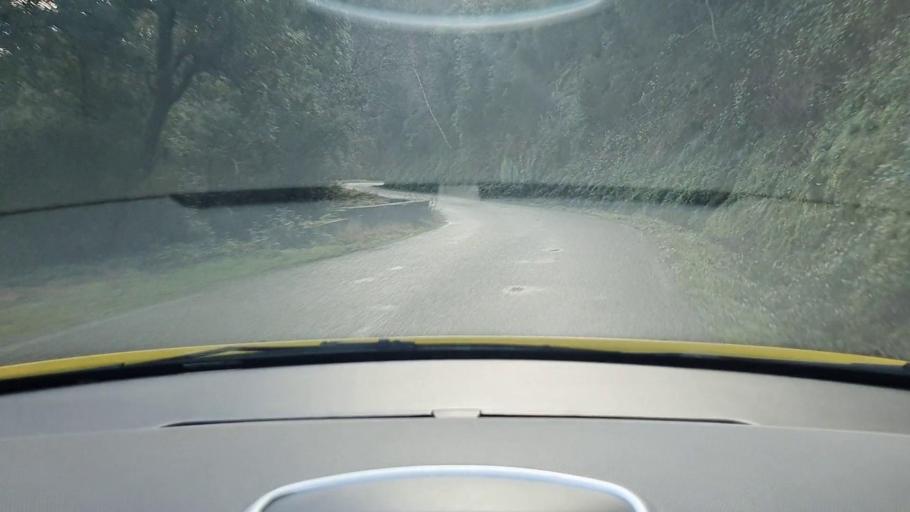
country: FR
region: Languedoc-Roussillon
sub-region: Departement du Gard
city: Branoux-les-Taillades
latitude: 44.2993
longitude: 3.9886
